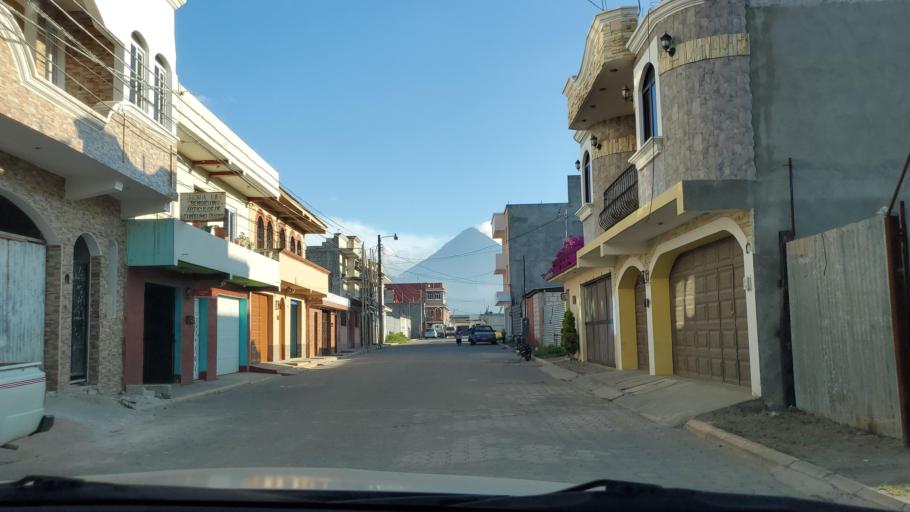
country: GT
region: Quetzaltenango
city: Quetzaltenango
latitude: 14.8362
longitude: -91.5457
